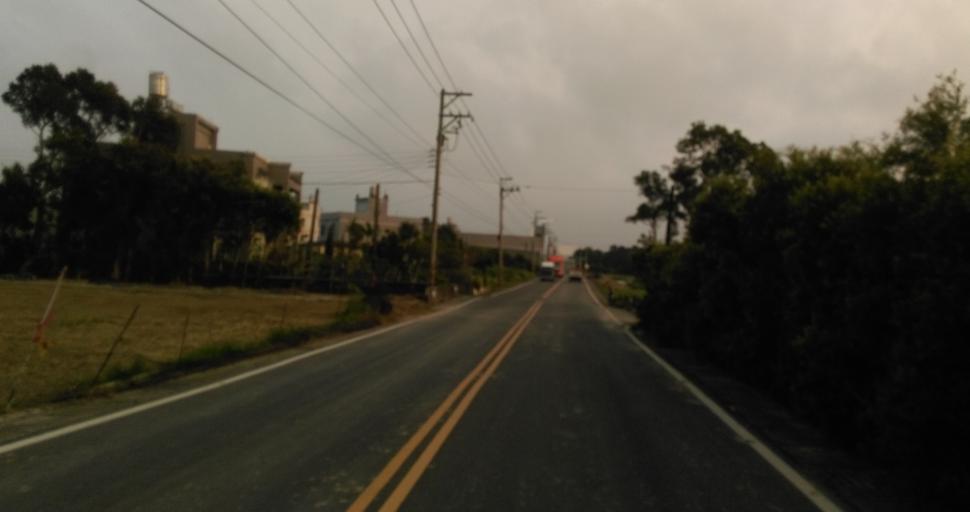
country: TW
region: Taiwan
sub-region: Hsinchu
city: Zhubei
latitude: 24.8651
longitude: 120.9599
